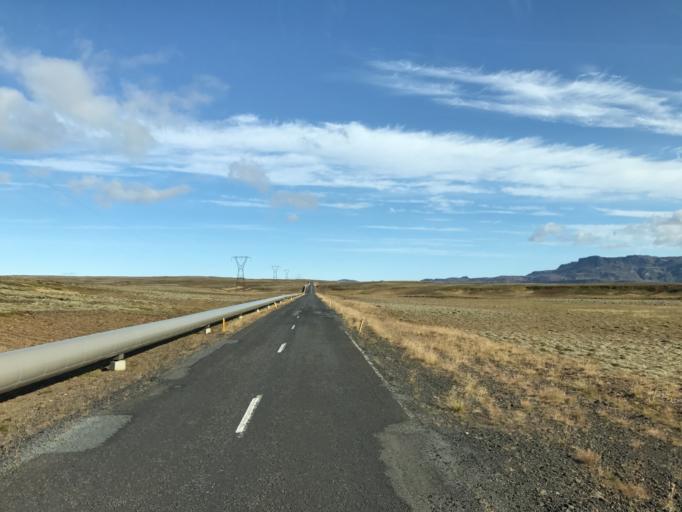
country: IS
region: Capital Region
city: Mosfellsbaer
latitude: 64.1144
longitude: -21.5092
